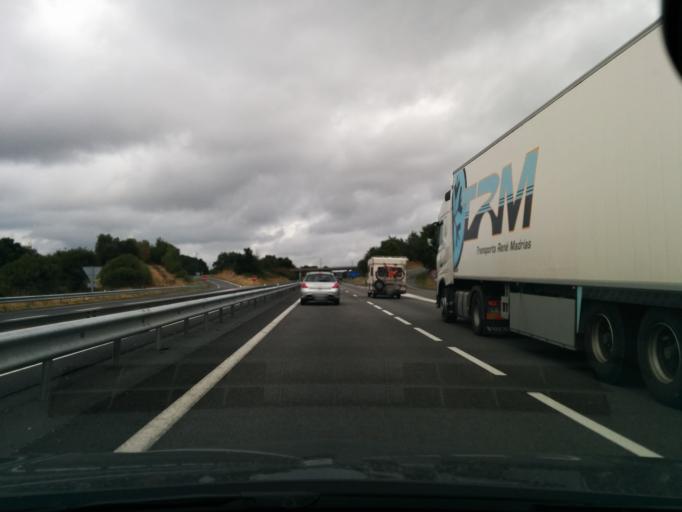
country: FR
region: Limousin
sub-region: Departement de la Haute-Vienne
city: Saint-Germain-les-Belles
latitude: 45.5246
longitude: 1.5151
